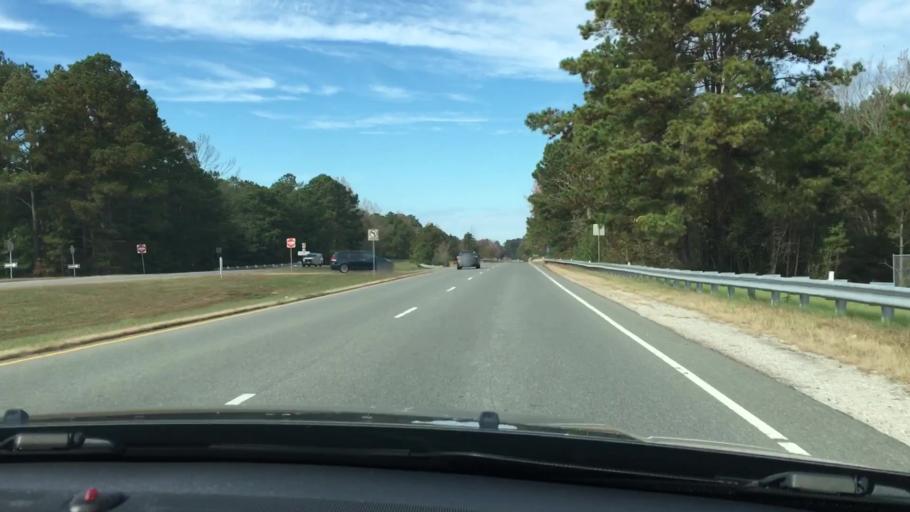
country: US
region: Virginia
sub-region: King William County
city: West Point
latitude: 37.4191
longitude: -76.8224
